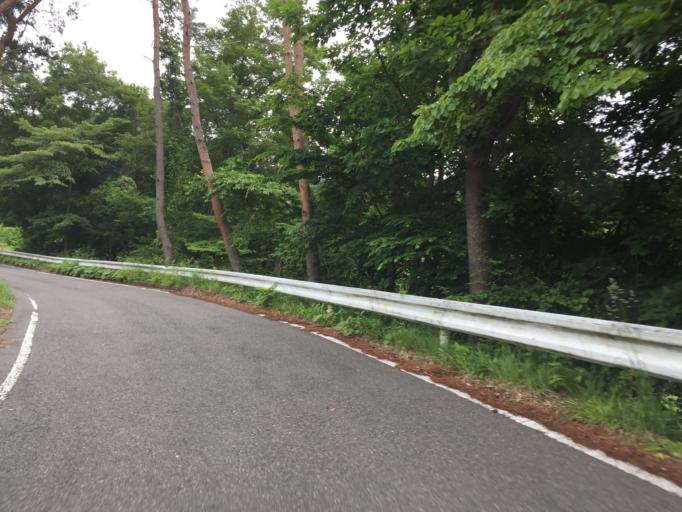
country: JP
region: Fukushima
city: Funehikimachi-funehiki
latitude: 37.3974
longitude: 140.6756
